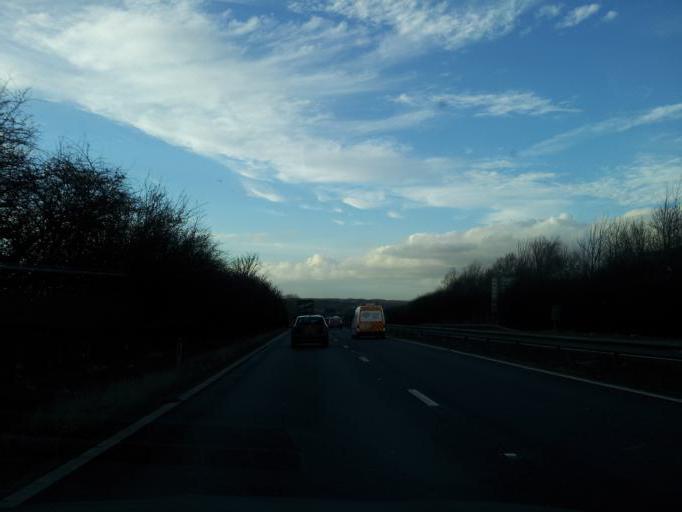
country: GB
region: England
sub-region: District of Rutland
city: Tinwell
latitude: 52.6596
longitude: -0.5176
